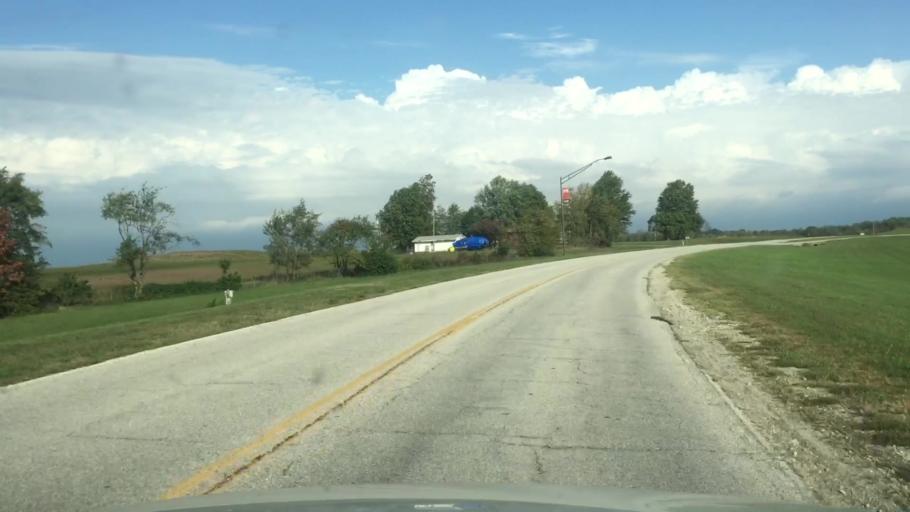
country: US
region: Missouri
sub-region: Boone County
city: Ashland
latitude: 38.8266
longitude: -92.2261
